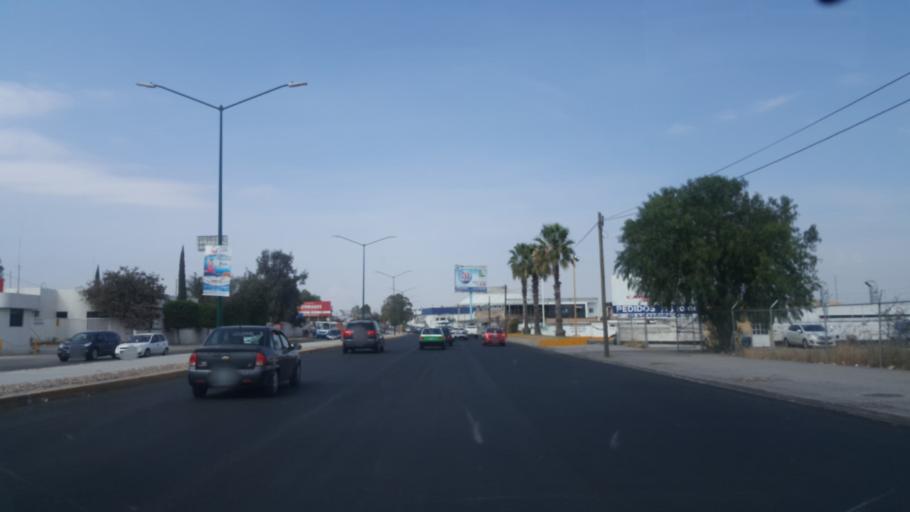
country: MX
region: Guanajuato
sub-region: Leon
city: Fraccionamiento Paraiso Real
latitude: 21.0953
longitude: -101.6296
